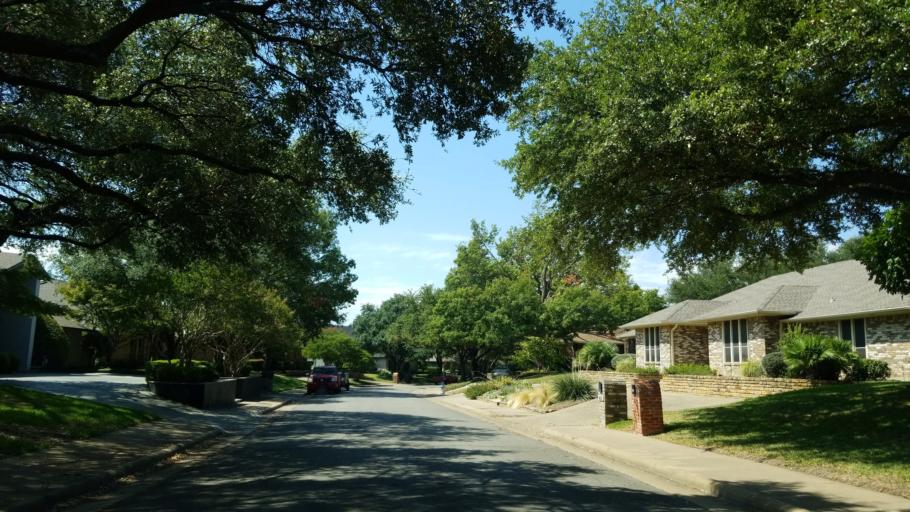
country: US
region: Texas
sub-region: Dallas County
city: Addison
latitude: 32.9645
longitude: -96.7996
